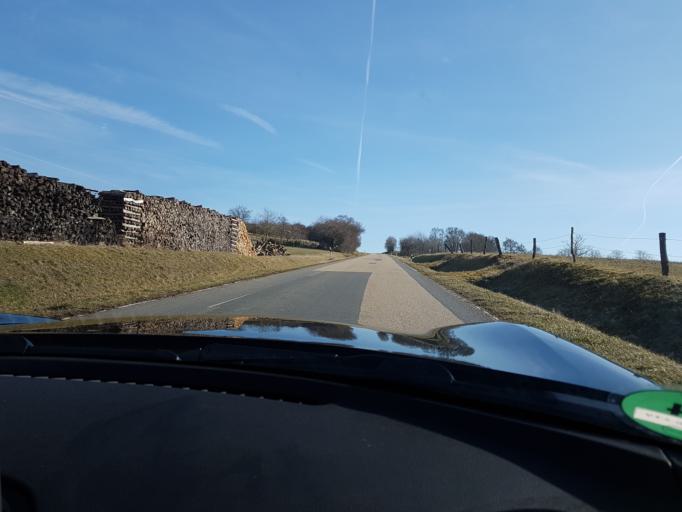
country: DE
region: Baden-Wuerttemberg
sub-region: Karlsruhe Region
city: Rosenberg
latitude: 49.4096
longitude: 9.5233
